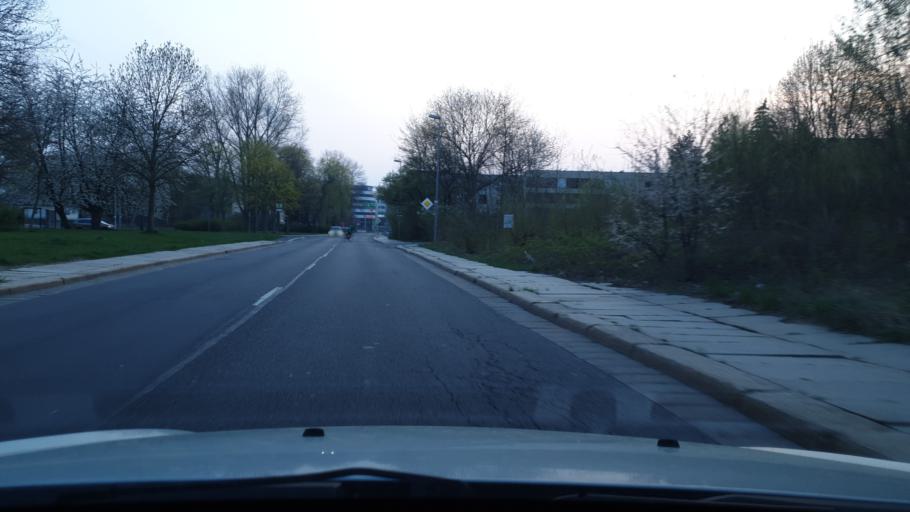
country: DE
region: Saxony
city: Chemnitz
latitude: 50.8318
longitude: 12.9445
